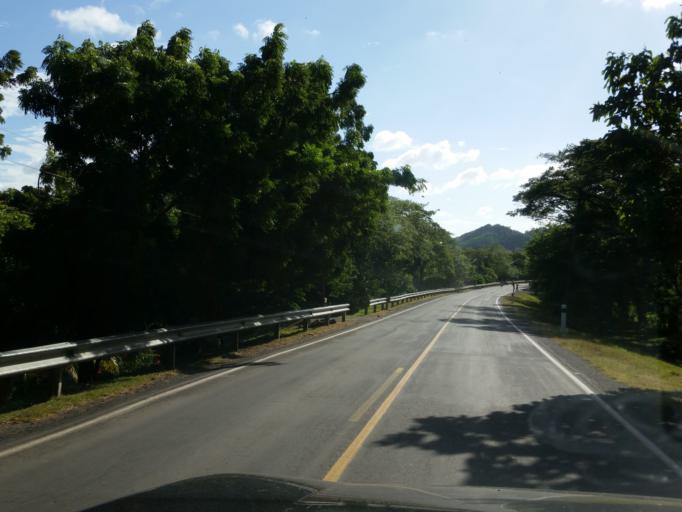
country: NI
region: Rivas
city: San Juan del Sur
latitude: 11.2675
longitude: -85.8473
